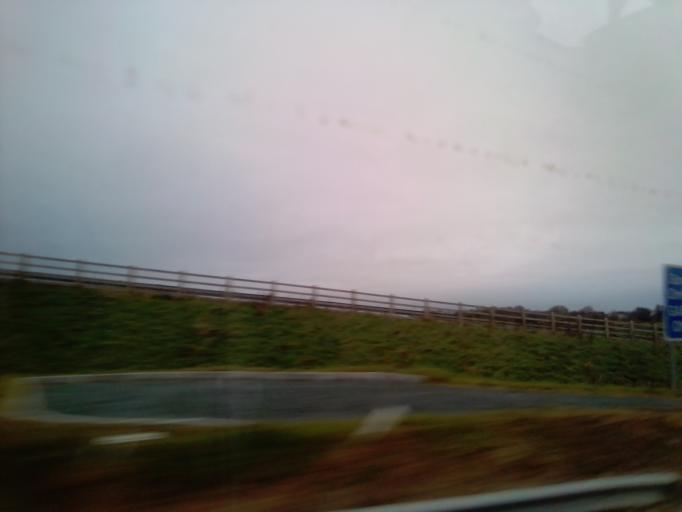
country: IE
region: Connaught
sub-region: County Galway
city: Athenry
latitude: 53.2565
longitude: -8.8268
